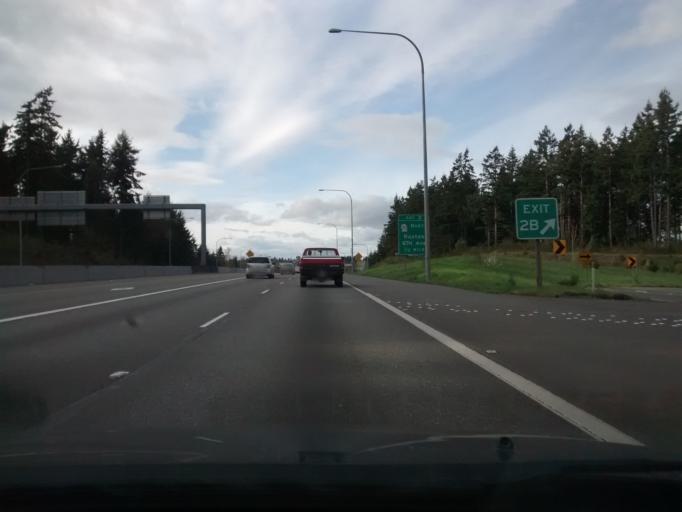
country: US
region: Washington
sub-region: Pierce County
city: Fircrest
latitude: 47.2452
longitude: -122.5065
